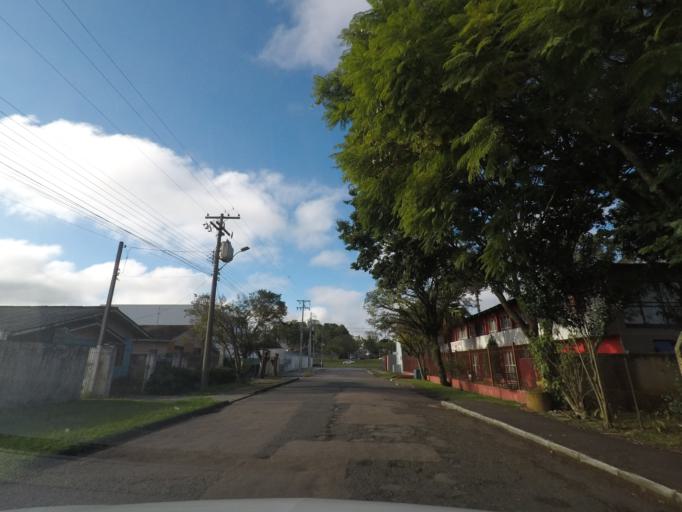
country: BR
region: Parana
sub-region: Curitiba
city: Curitiba
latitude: -25.4515
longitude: -49.2413
